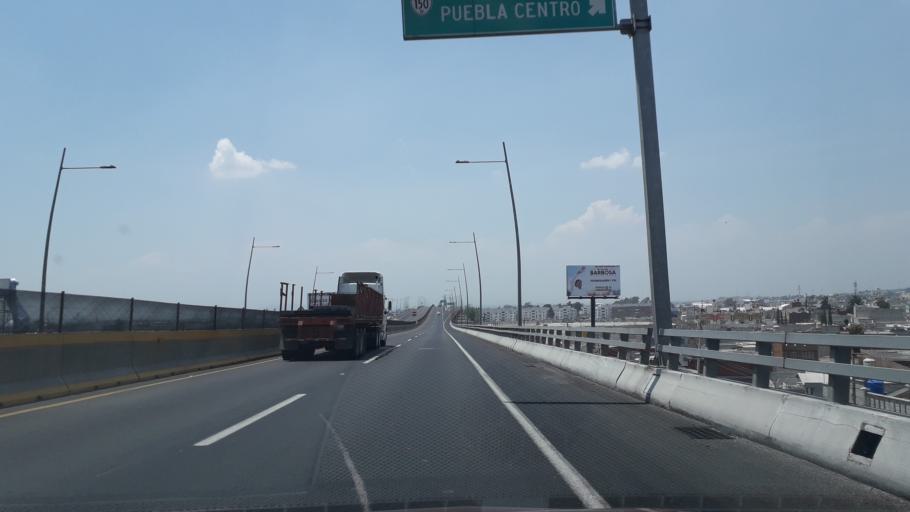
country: MX
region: Puebla
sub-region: Puebla
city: San Sebastian de Aparicio
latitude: 19.0818
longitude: -98.1740
